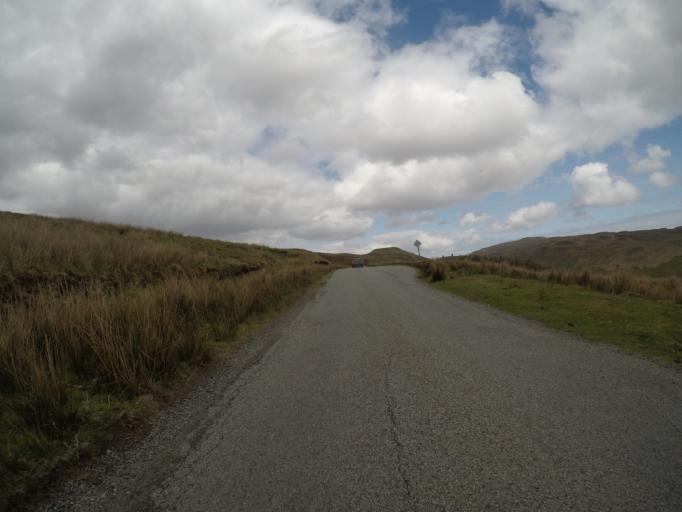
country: GB
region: Scotland
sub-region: Highland
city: Isle of Skye
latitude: 57.3700
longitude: -6.3820
